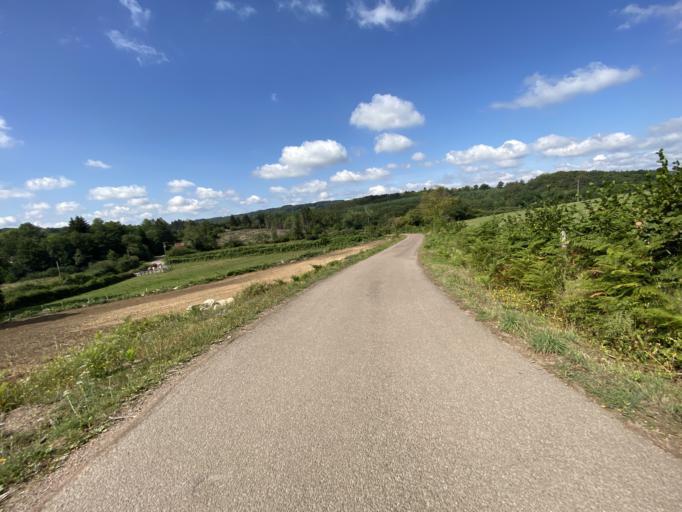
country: FR
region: Bourgogne
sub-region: Departement de la Cote-d'Or
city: Saulieu
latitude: 47.2690
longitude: 4.1553
